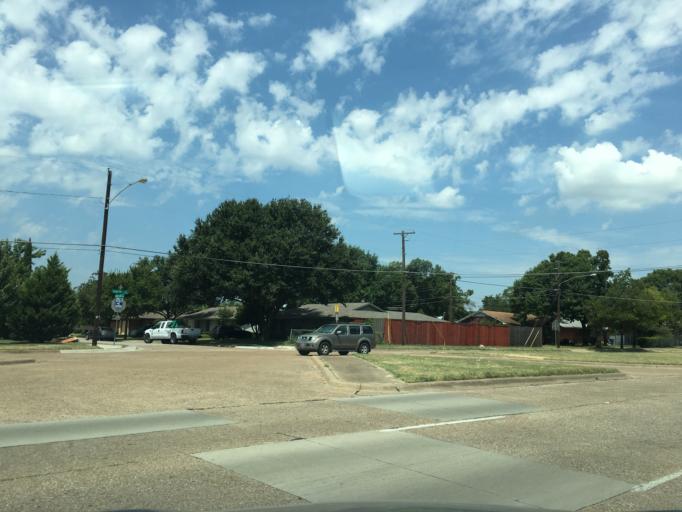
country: US
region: Texas
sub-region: Dallas County
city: Garland
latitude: 32.8566
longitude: -96.6829
